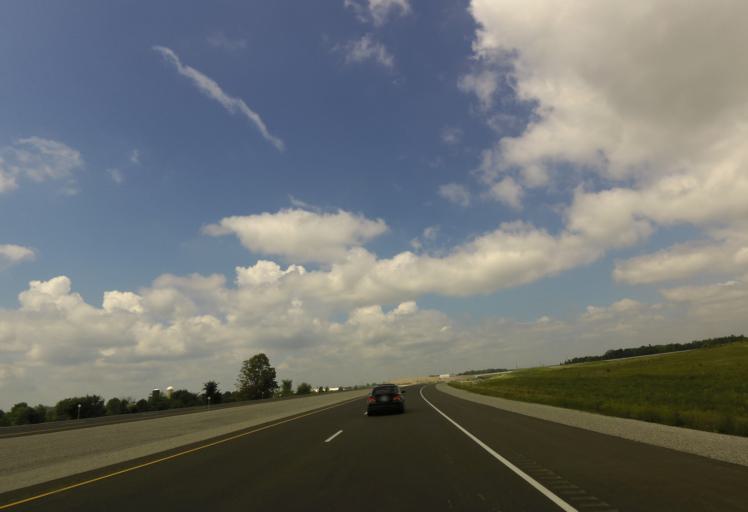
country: CA
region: Ontario
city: Ajax
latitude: 43.8825
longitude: -78.9845
